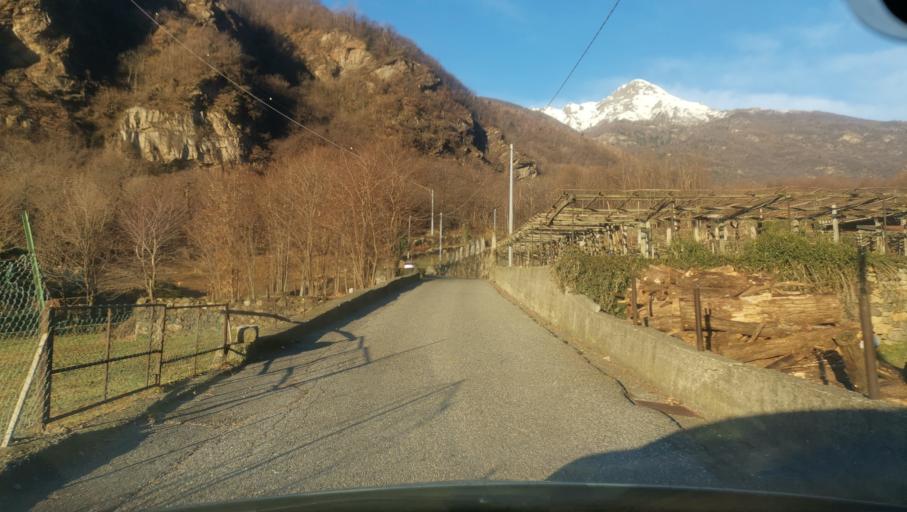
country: IT
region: Piedmont
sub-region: Provincia di Torino
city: Tavagnasco
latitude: 45.5461
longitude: 7.8196
